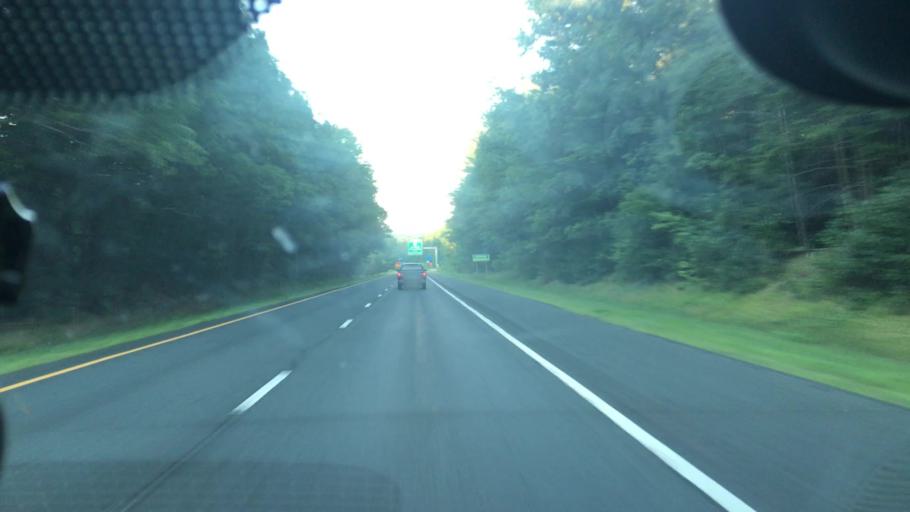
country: US
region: Massachusetts
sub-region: Franklin County
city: Bernardston
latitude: 42.6541
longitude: -72.5542
